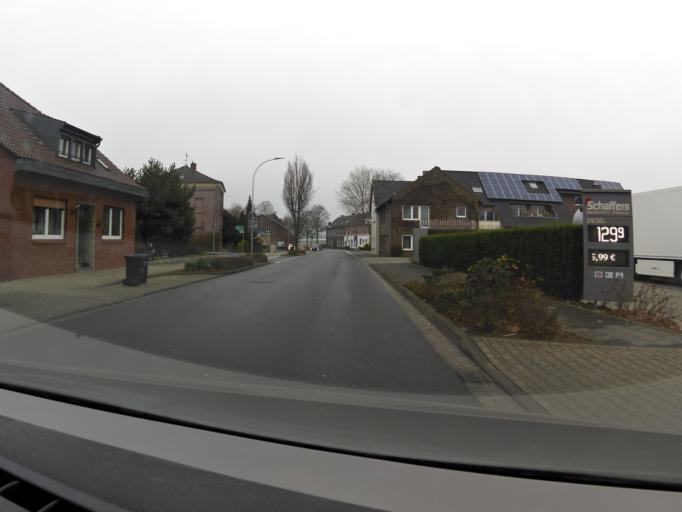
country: DE
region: North Rhine-Westphalia
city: Straelen
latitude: 51.4090
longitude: 6.2633
